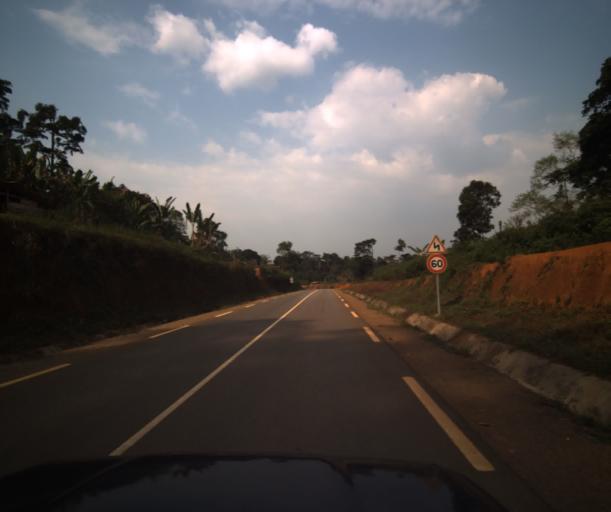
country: CM
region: Centre
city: Mbankomo
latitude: 3.6667
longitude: 11.3439
